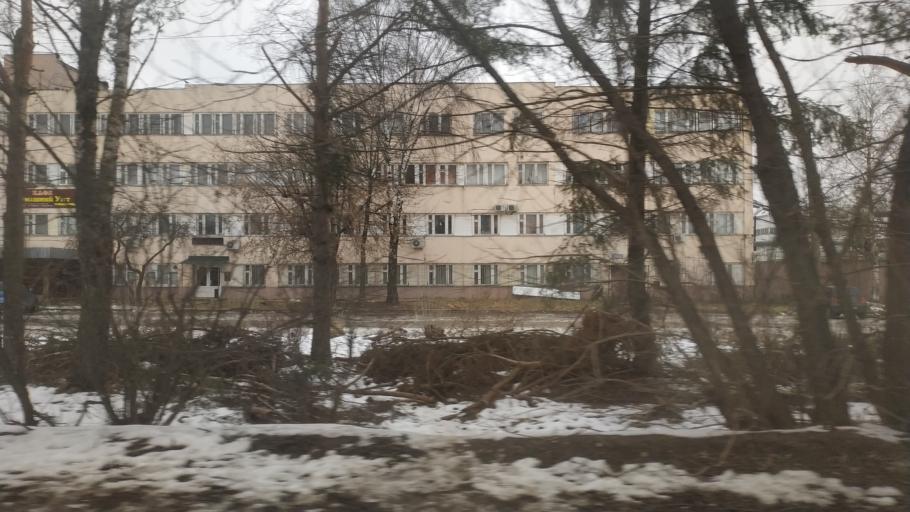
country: RU
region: Tverskaya
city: Tver
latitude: 56.8928
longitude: 35.8382
